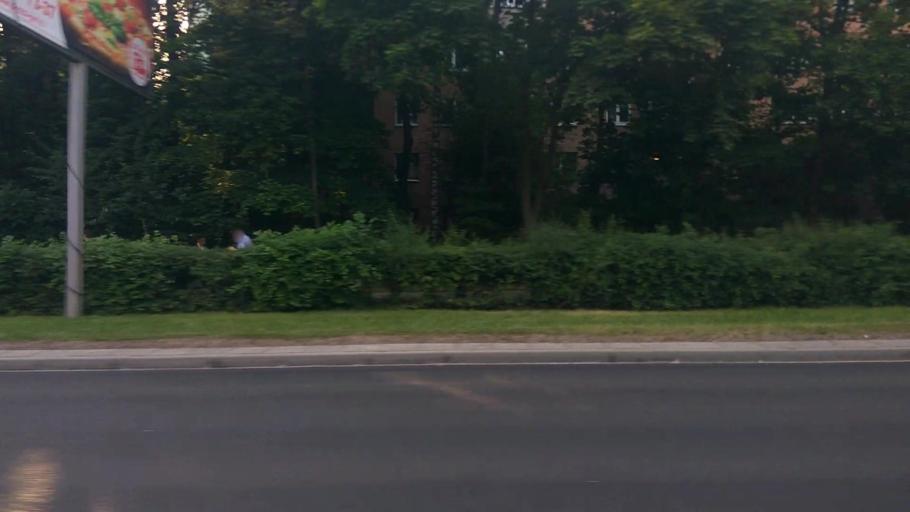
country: RU
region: Moskovskaya
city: Mytishchi
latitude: 55.9146
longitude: 37.7440
